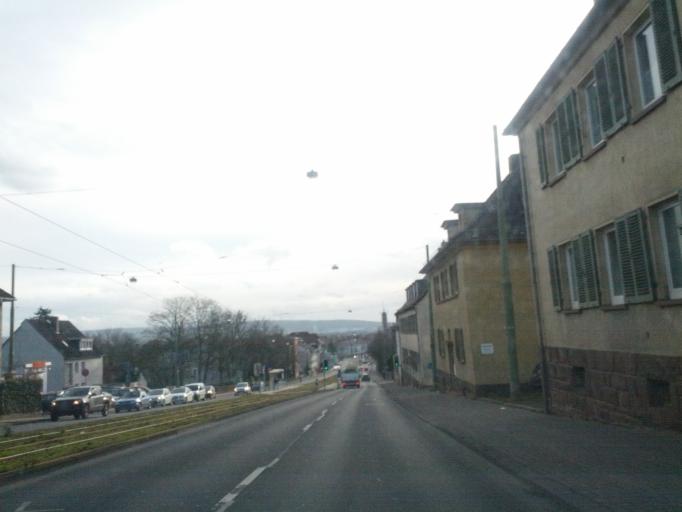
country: DE
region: Hesse
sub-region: Regierungsbezirk Kassel
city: Kassel
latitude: 51.3285
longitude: 9.5133
